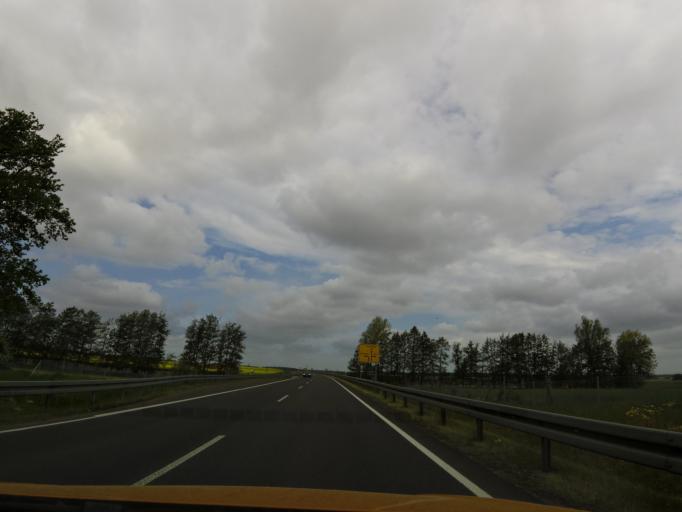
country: DE
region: Brandenburg
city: Niemegk
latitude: 52.1042
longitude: 12.6785
